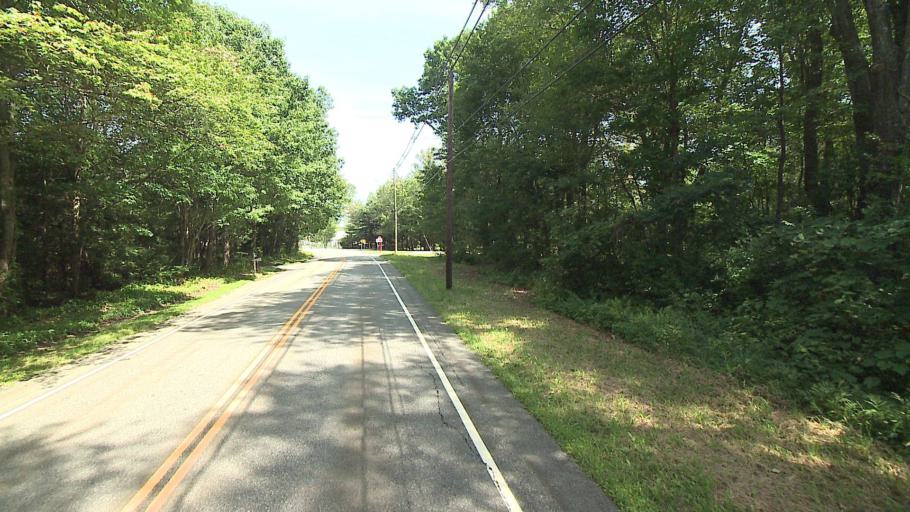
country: US
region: Connecticut
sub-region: Litchfield County
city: Bethlehem Village
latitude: 41.6592
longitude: -73.1986
